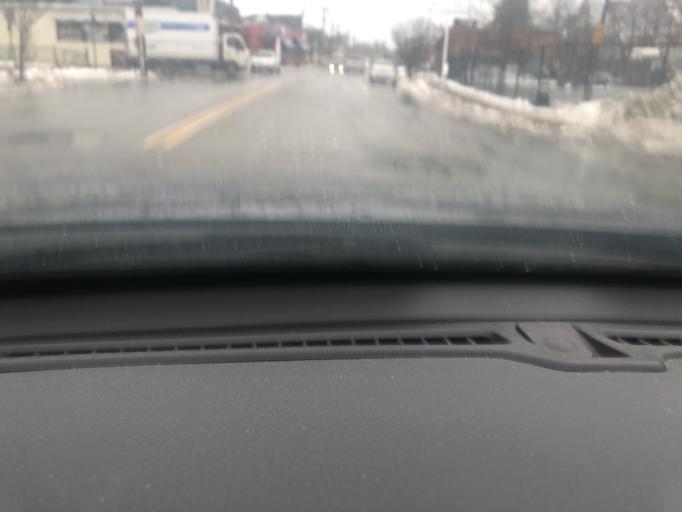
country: US
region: Massachusetts
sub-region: Plymouth County
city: Brockton
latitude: 42.1037
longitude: -71.0236
